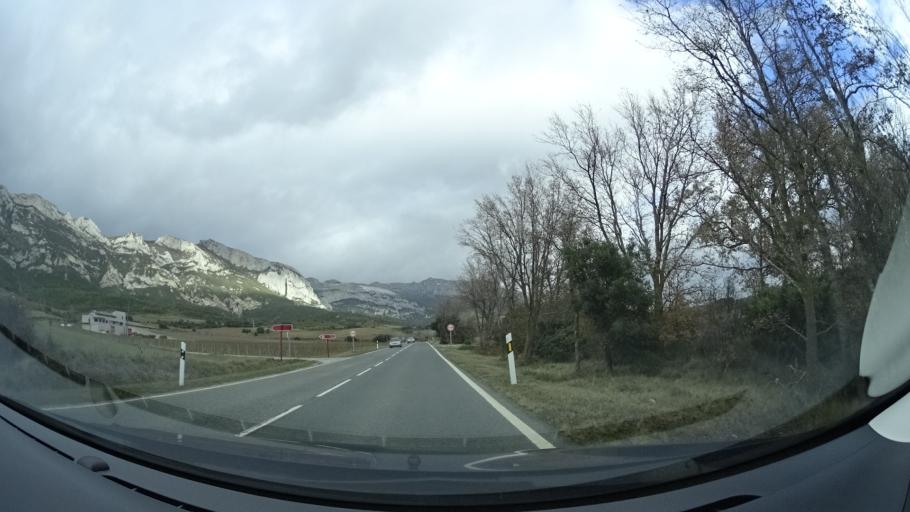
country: ES
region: Basque Country
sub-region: Provincia de Alava
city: Leza
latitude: 42.5749
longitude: -2.6517
